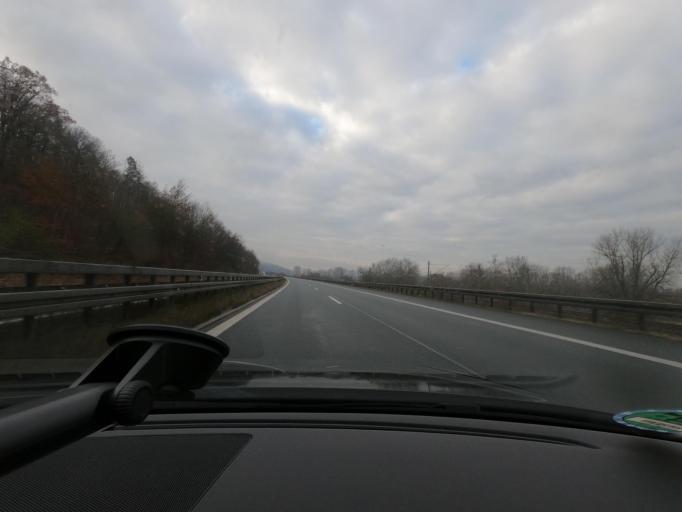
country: DE
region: Bavaria
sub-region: Upper Franconia
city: Zapfendorf
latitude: 49.9993
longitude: 10.9123
